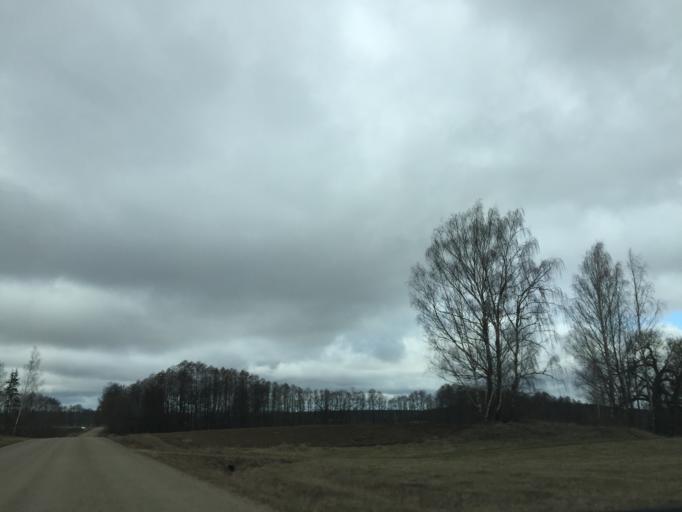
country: LV
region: Ilukste
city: Ilukste
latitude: 56.0592
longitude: 26.1684
